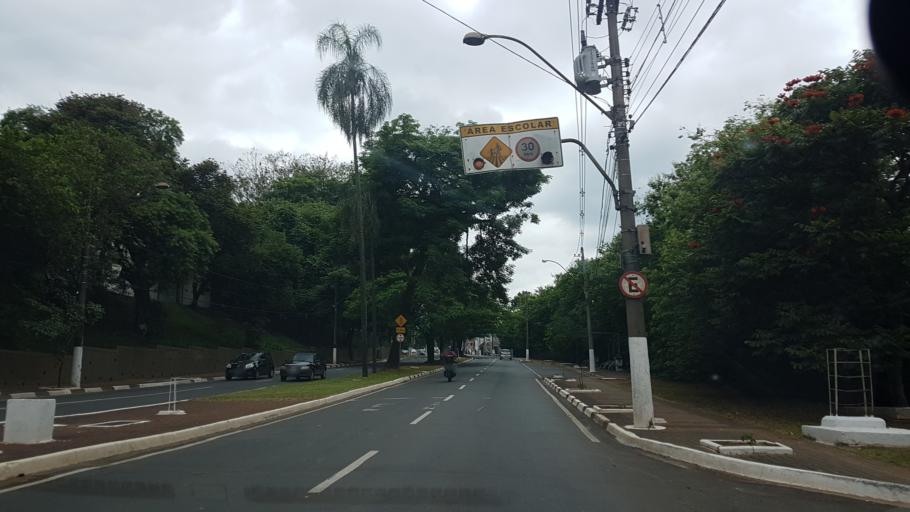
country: BR
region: Sao Paulo
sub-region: Paulinia
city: Paulinia
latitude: -22.7580
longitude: -47.1603
